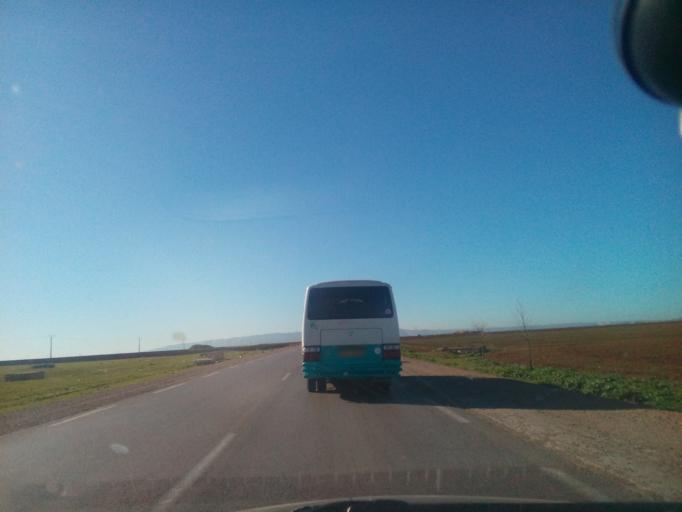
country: DZ
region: Relizane
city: Relizane
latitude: 35.8932
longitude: 0.6391
